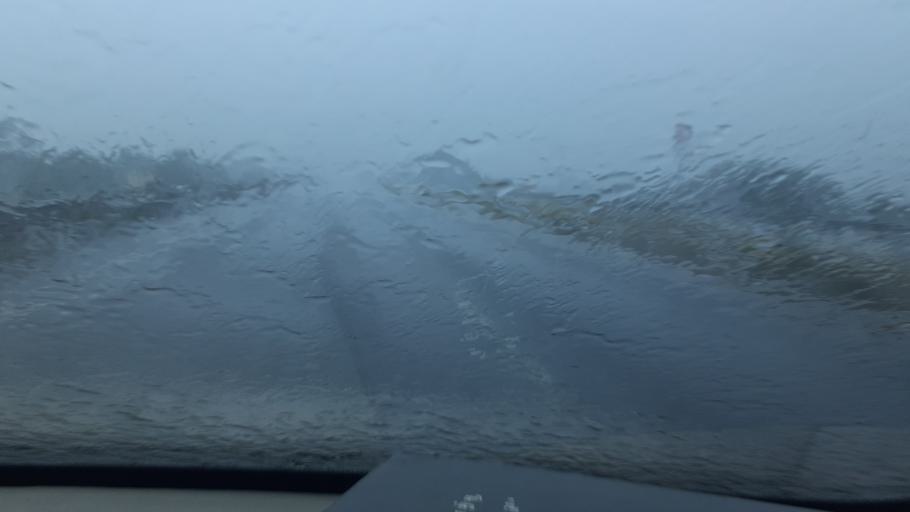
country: IN
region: Tamil Nadu
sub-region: Virudhunagar
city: Sattur
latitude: 9.4533
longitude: 77.9298
